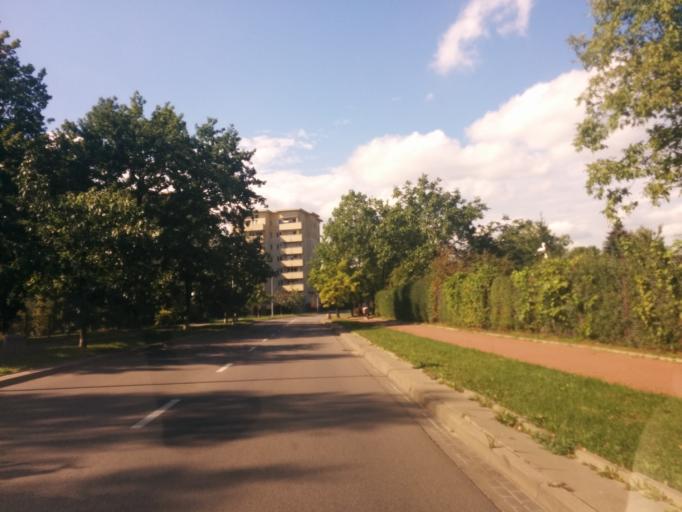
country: PL
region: Masovian Voivodeship
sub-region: Warszawa
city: Bialoleka
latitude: 52.3231
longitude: 20.9626
